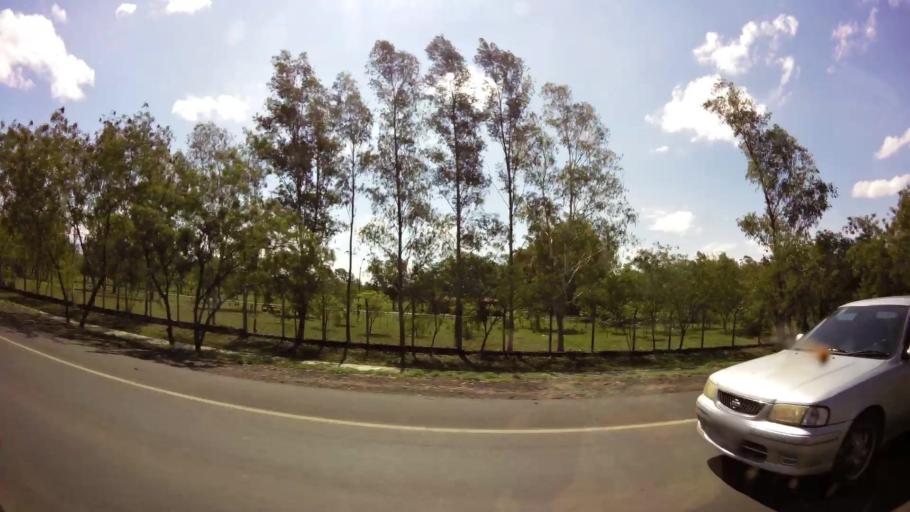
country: PY
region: Central
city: Fernando de la Mora
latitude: -25.2679
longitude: -57.5366
